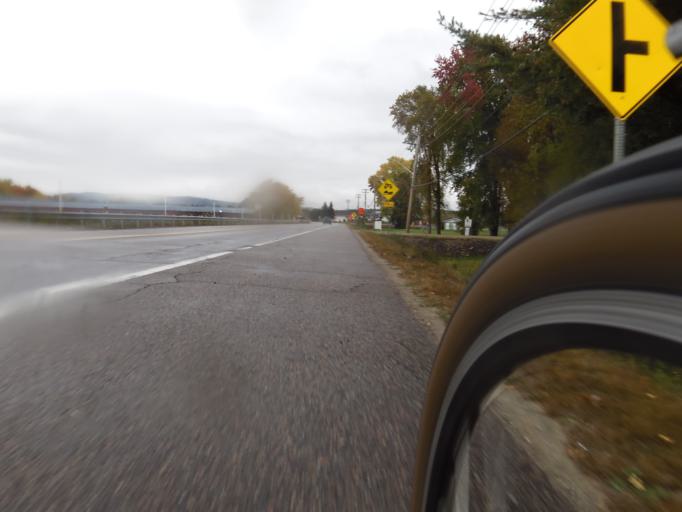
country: CA
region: Quebec
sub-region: Outaouais
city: Fort-Coulonge
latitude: 45.8590
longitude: -76.7396
